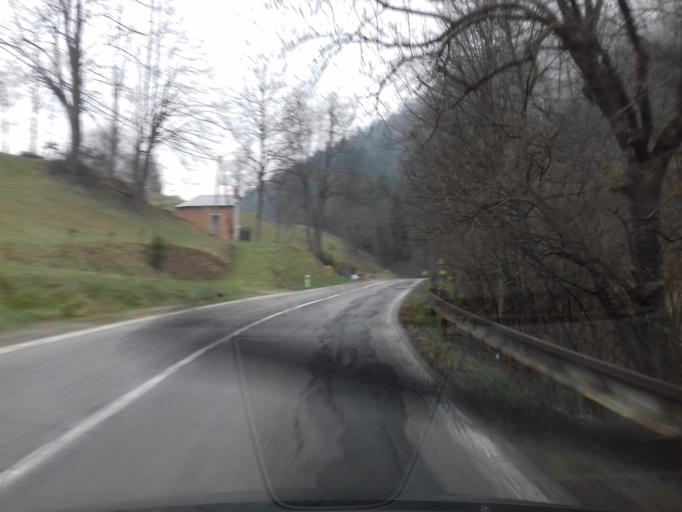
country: PL
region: Lesser Poland Voivodeship
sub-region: Powiat nowosadecki
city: Piwniczna-Zdroj
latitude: 49.3972
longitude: 20.7002
